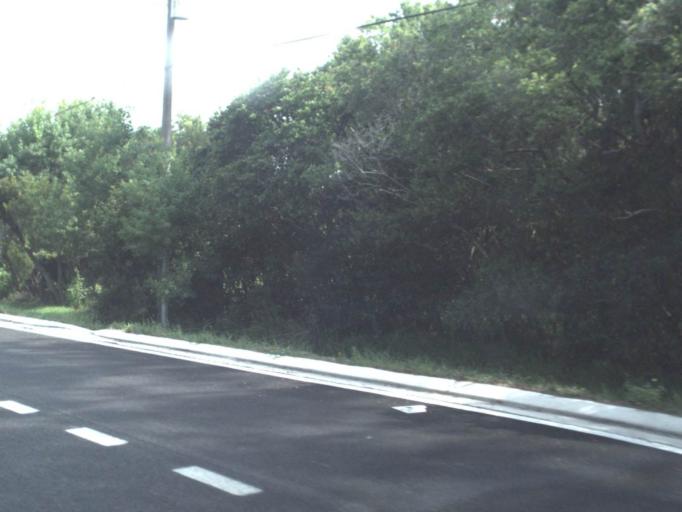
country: US
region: Florida
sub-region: Nassau County
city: Nassau Village-Ratliff
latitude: 30.5244
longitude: -81.8015
